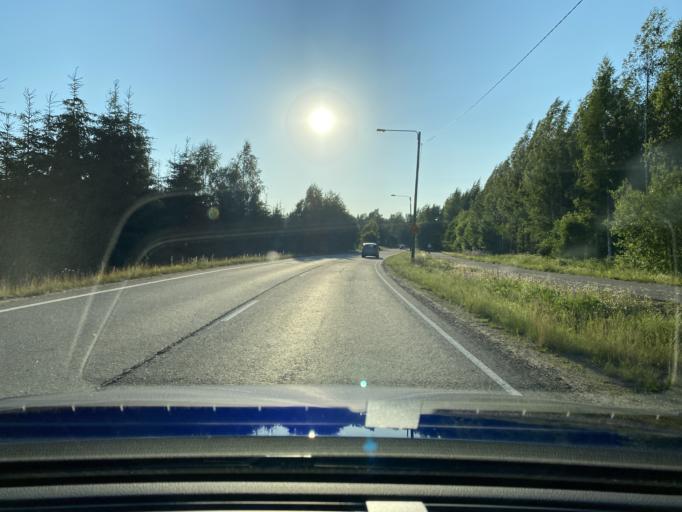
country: FI
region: Haeme
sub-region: Riihimaeki
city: Riihimaeki
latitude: 60.7175
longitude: 24.7126
